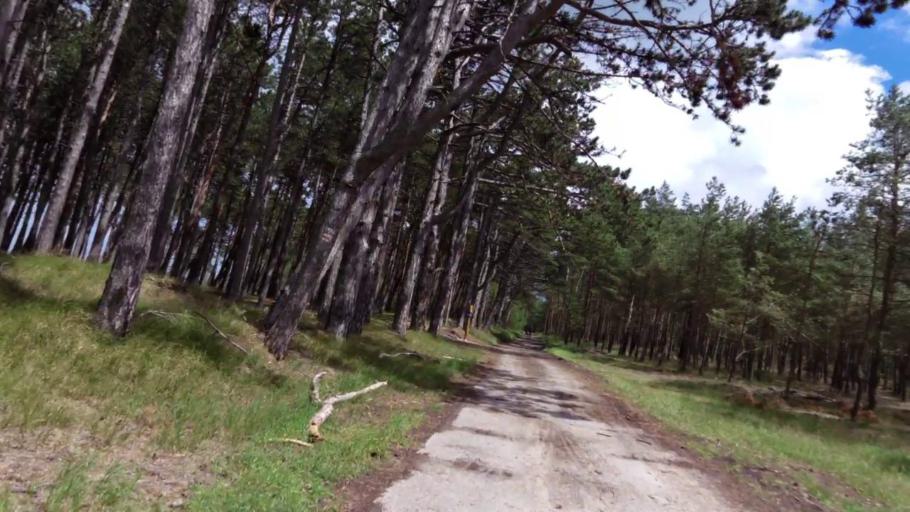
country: PL
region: West Pomeranian Voivodeship
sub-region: Powiat slawienski
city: Darlowo
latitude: 54.4987
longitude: 16.4522
